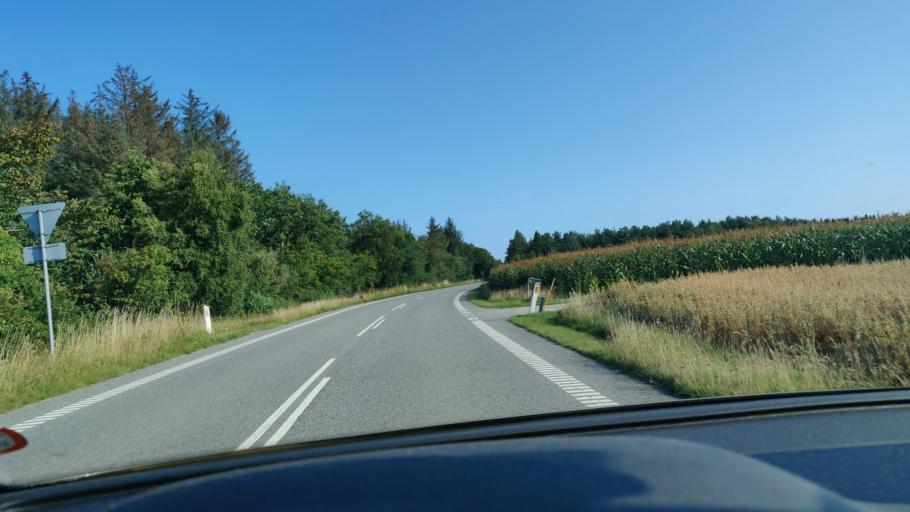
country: DK
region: North Denmark
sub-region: Jammerbugt Kommune
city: Pandrup
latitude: 57.2476
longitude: 9.6455
